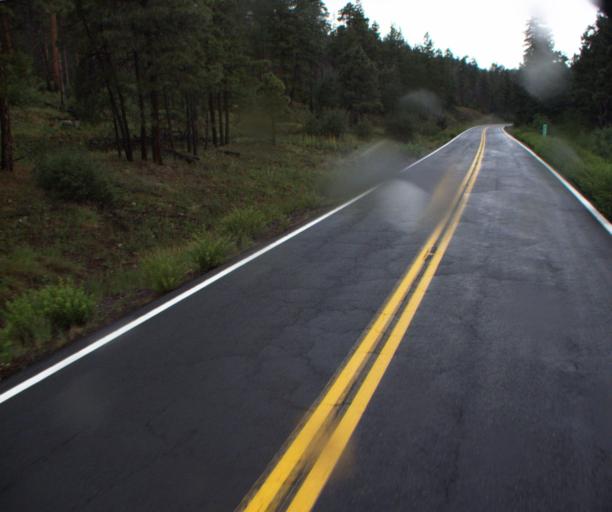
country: US
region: Arizona
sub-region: Apache County
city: Eagar
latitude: 33.7249
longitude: -109.1988
